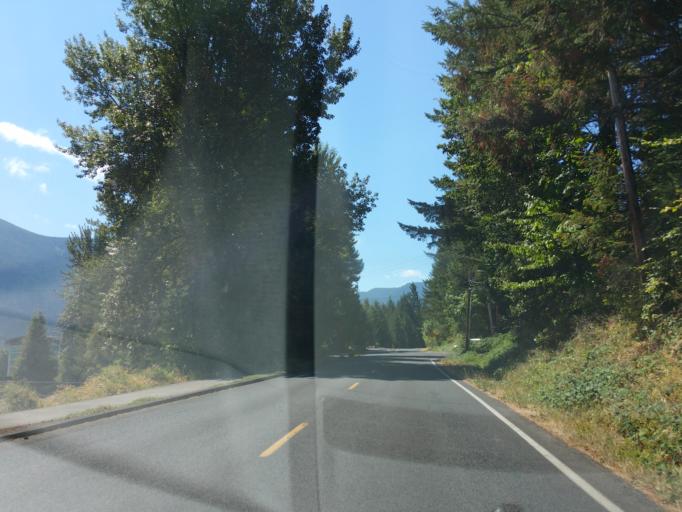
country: US
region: Washington
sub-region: Skamania County
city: Stevenson
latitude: 45.6873
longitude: -121.8997
